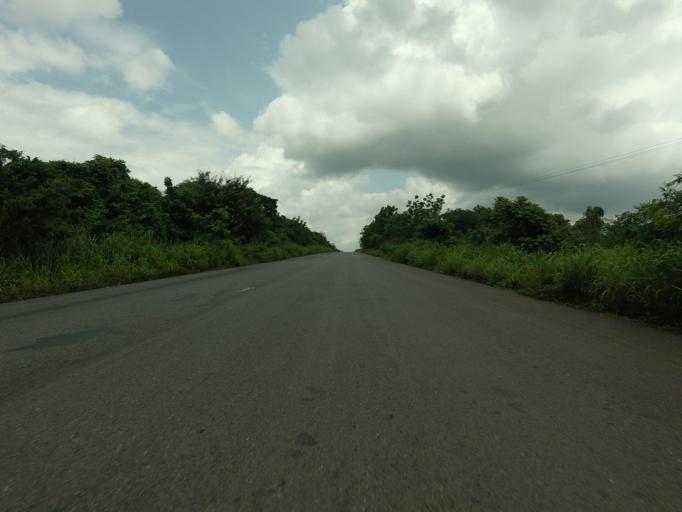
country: GH
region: Volta
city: Ho
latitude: 6.6111
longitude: 0.3002
